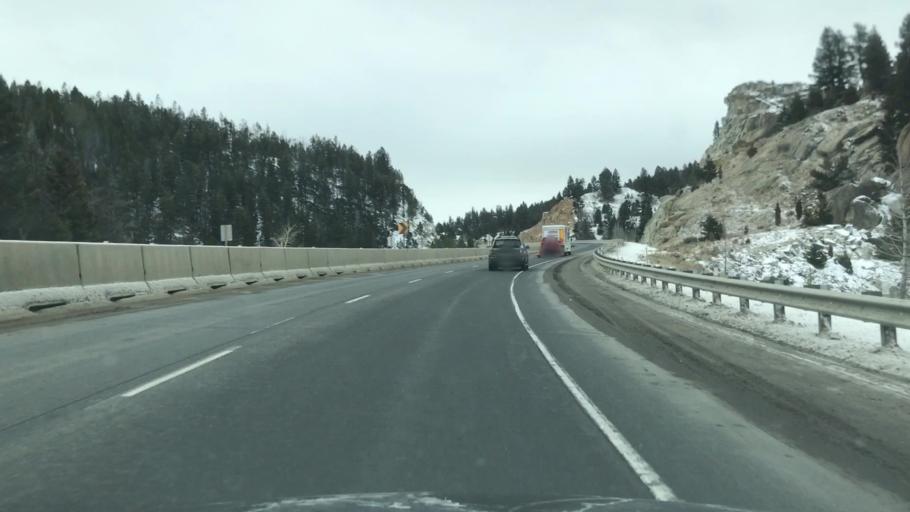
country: US
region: Montana
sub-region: Silver Bow County
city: Butte
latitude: 45.9109
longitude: -112.3383
